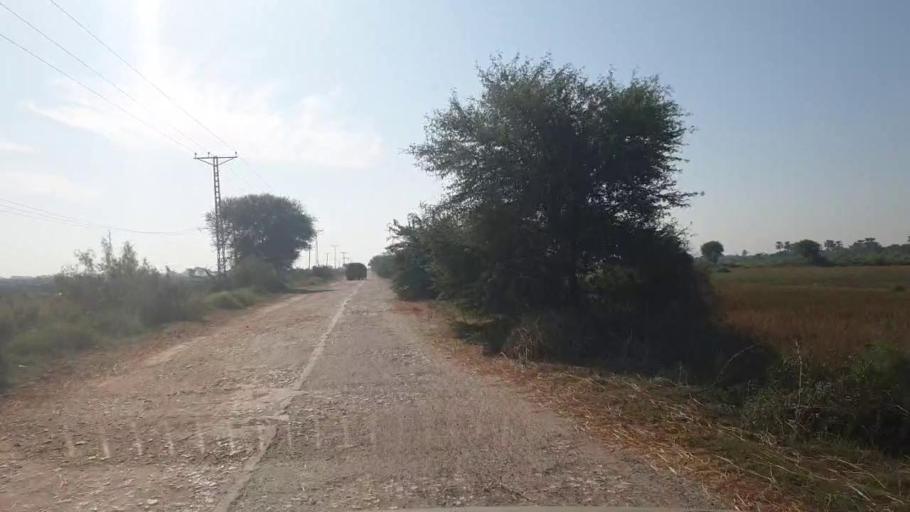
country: PK
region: Sindh
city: Talhar
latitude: 24.9162
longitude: 68.8163
